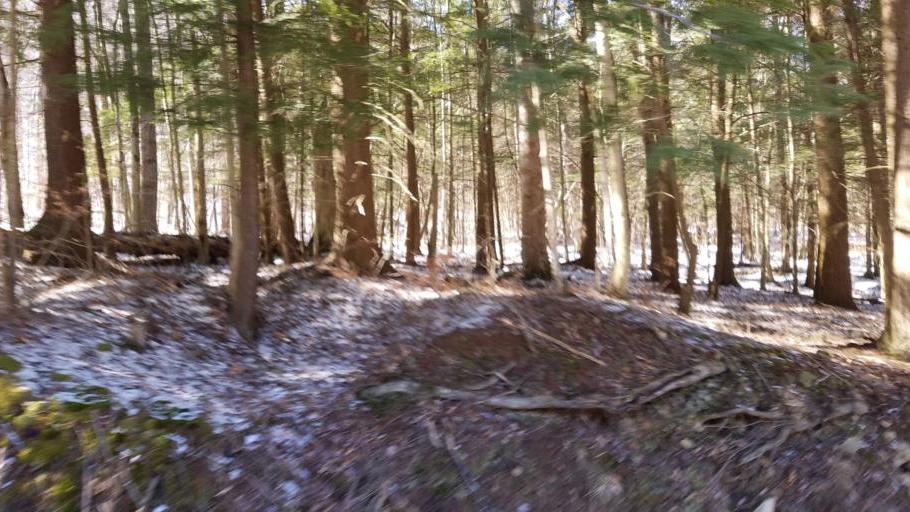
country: US
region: New York
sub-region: Allegany County
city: Wellsville
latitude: 42.0175
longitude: -77.9262
